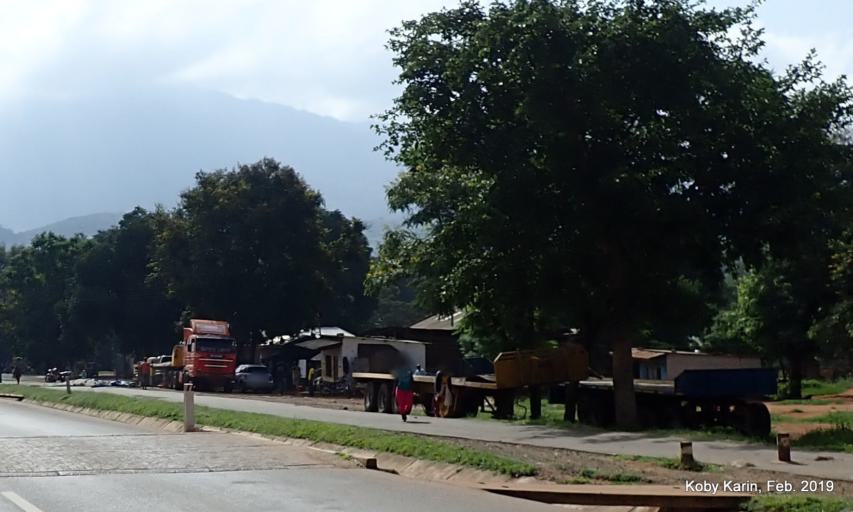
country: TZ
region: Manyara
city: Babati
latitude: -4.2147
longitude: 35.7413
